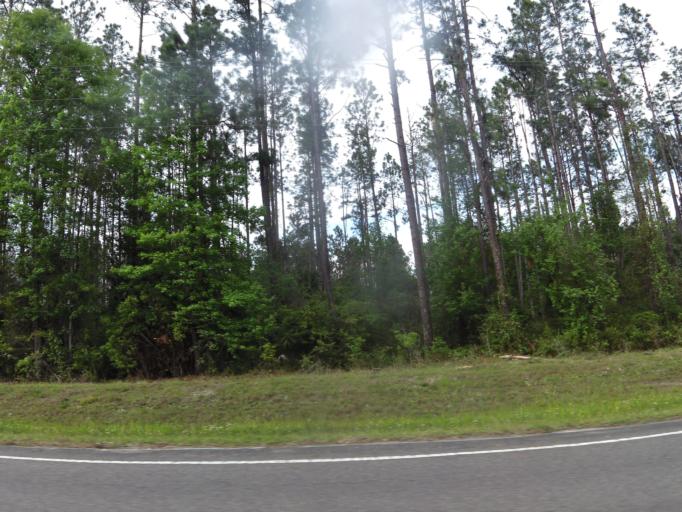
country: US
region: Florida
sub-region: Nassau County
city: Hilliard
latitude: 30.6950
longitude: -81.8576
